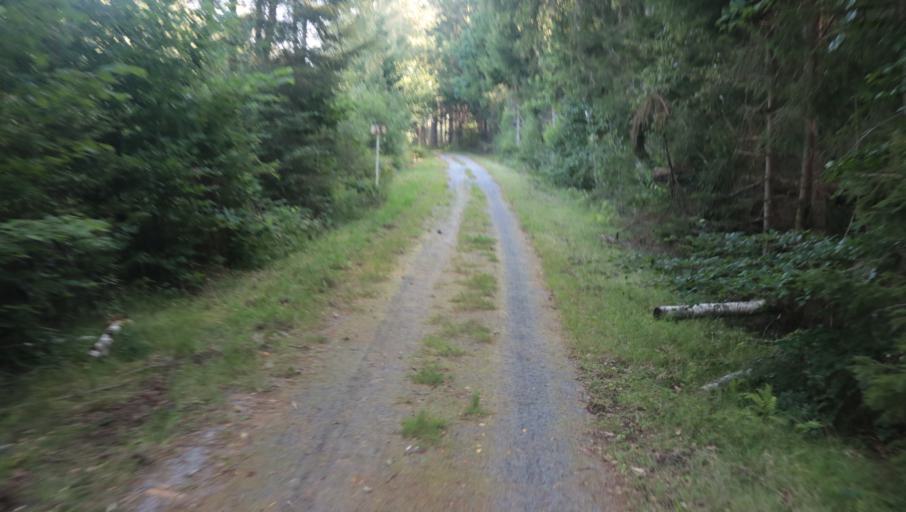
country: SE
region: Blekinge
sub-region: Karlshamns Kommun
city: Svangsta
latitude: 56.3105
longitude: 14.7177
